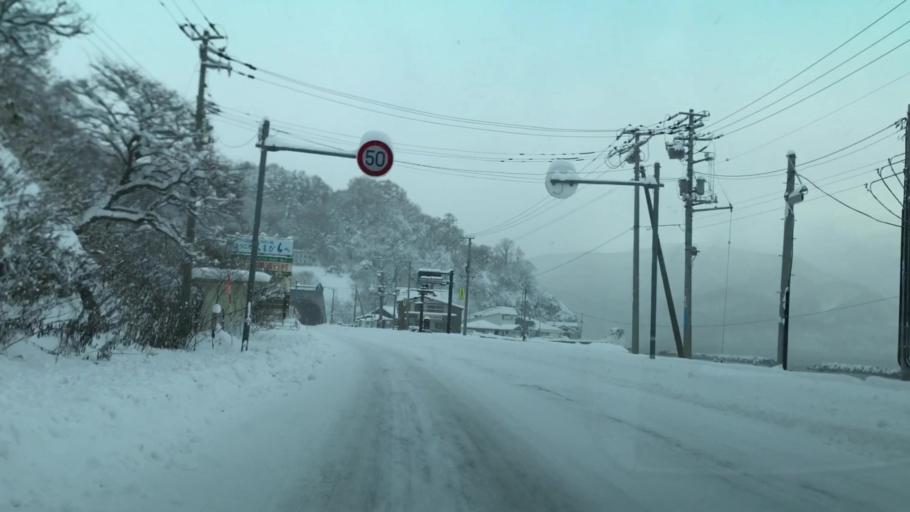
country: JP
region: Hokkaido
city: Yoichi
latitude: 43.2598
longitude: 140.6566
